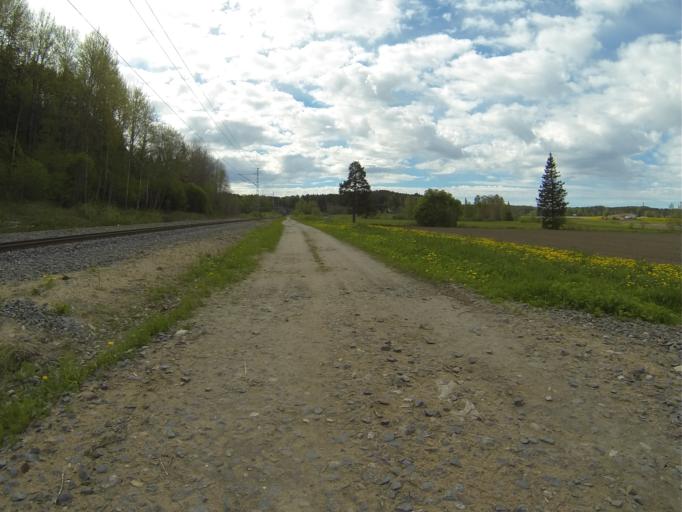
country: FI
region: Varsinais-Suomi
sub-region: Salo
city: Salo
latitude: 60.3623
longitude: 23.1181
